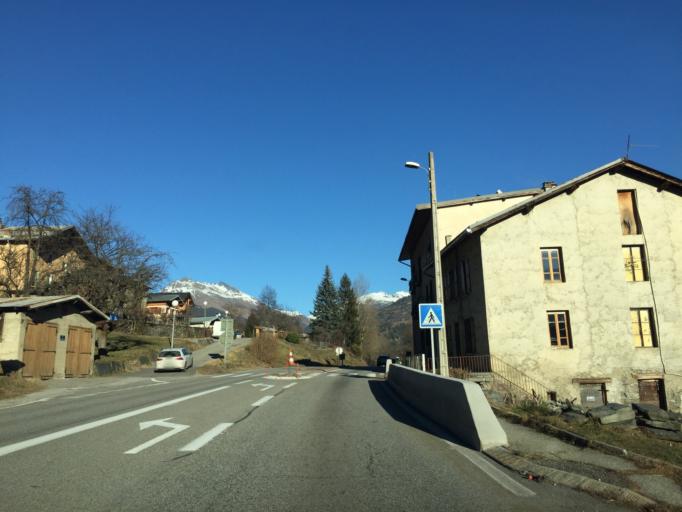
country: FR
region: Rhone-Alpes
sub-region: Departement de la Savoie
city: Bourg-Saint-Maurice
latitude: 45.5831
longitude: 6.7399
